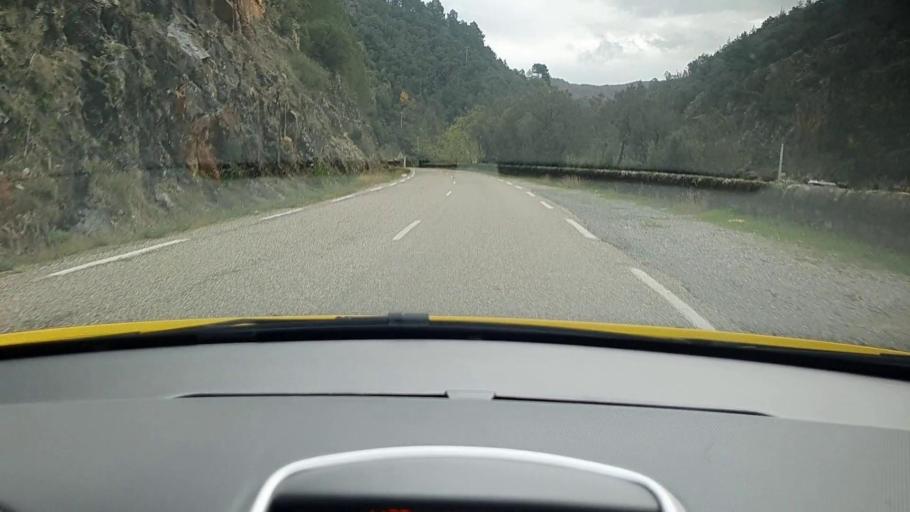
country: FR
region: Languedoc-Roussillon
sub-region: Departement du Gard
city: Lasalle
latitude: 44.1064
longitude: 3.7893
